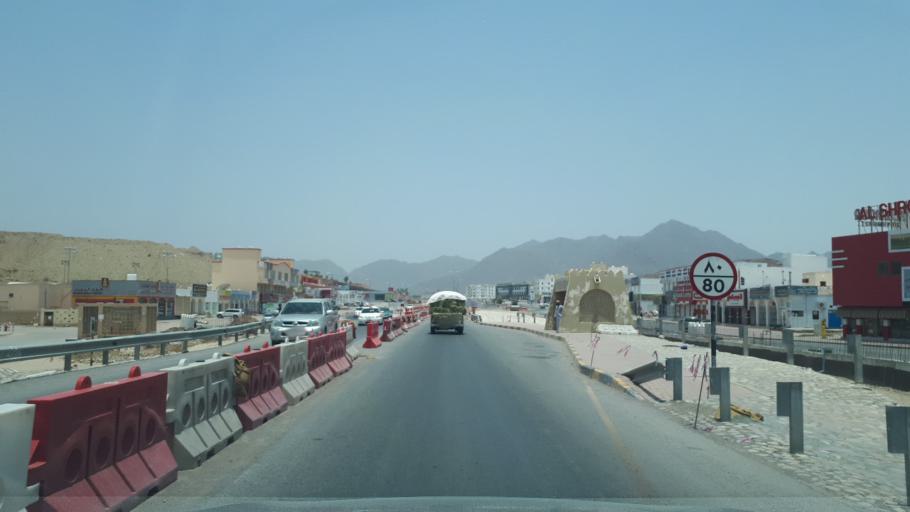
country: OM
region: Al Batinah
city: Rustaq
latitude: 23.4321
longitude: 57.4233
